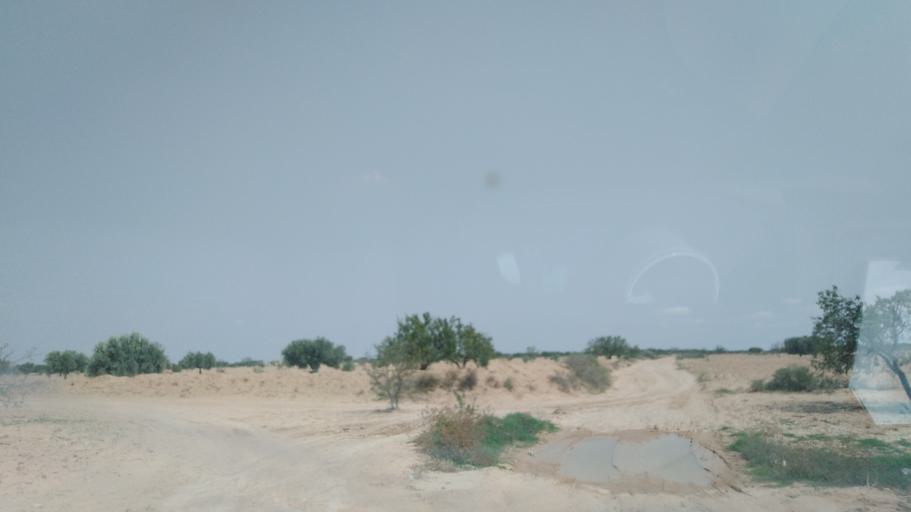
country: TN
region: Safaqis
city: Sfax
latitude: 34.6467
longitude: 10.5586
